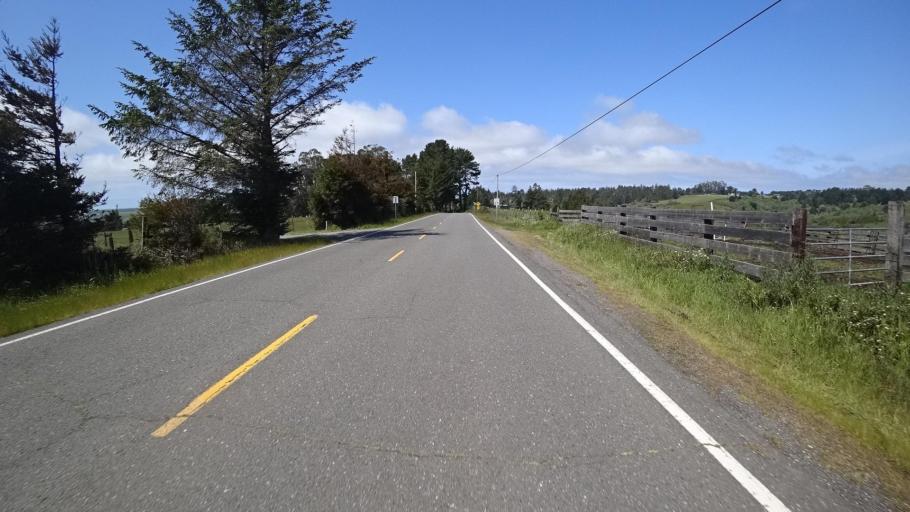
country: US
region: California
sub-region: Humboldt County
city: Fortuna
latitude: 40.6445
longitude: -124.2131
